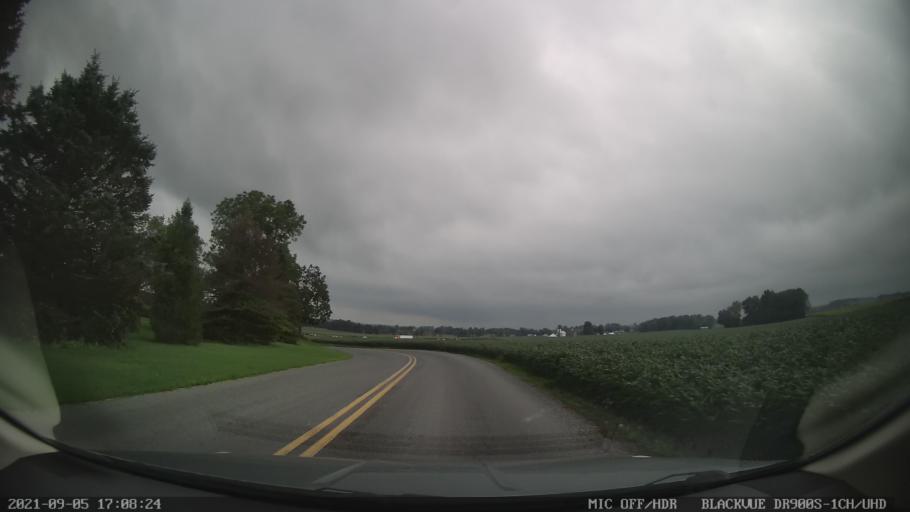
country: US
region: Pennsylvania
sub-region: Lehigh County
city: Breinigsville
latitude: 40.5481
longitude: -75.6794
